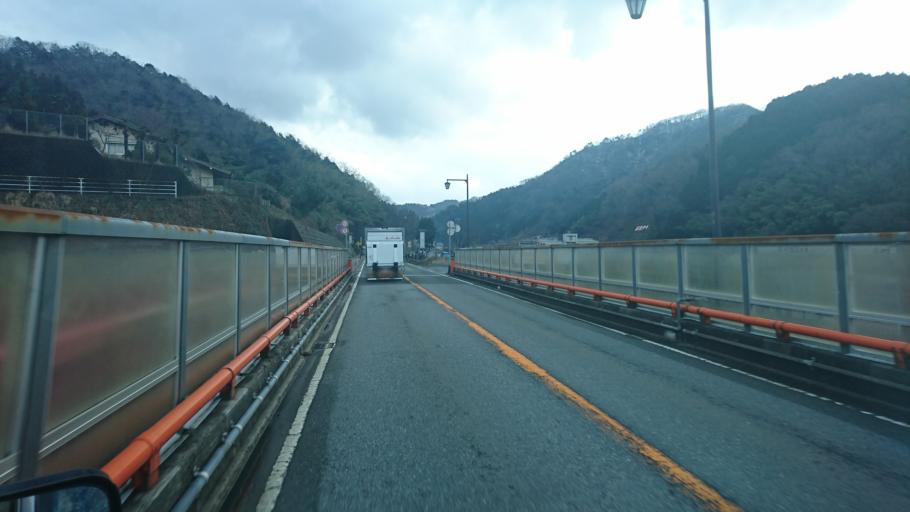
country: JP
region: Tottori
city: Tottori
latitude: 35.5553
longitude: 134.4904
